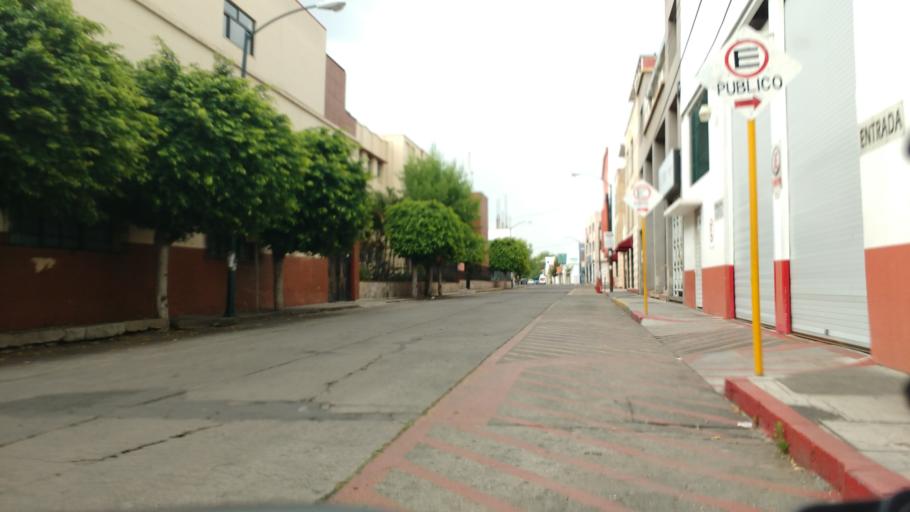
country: MX
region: Michoacan
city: Morelia
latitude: 19.6957
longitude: -101.1836
